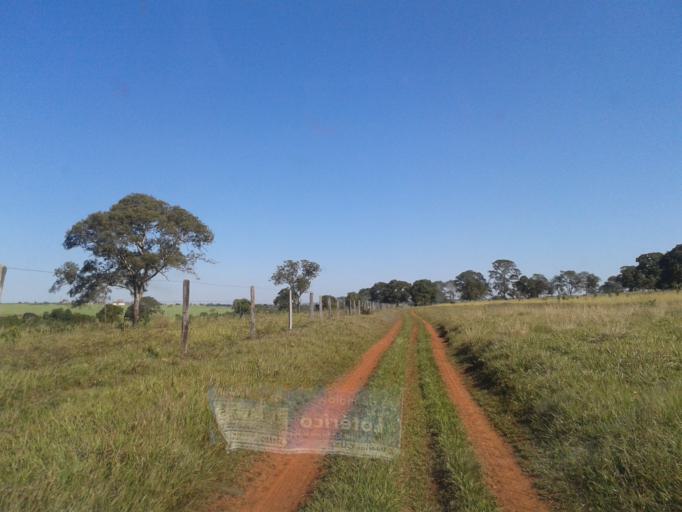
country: BR
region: Minas Gerais
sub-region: Santa Vitoria
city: Santa Vitoria
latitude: -19.0362
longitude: -50.3791
